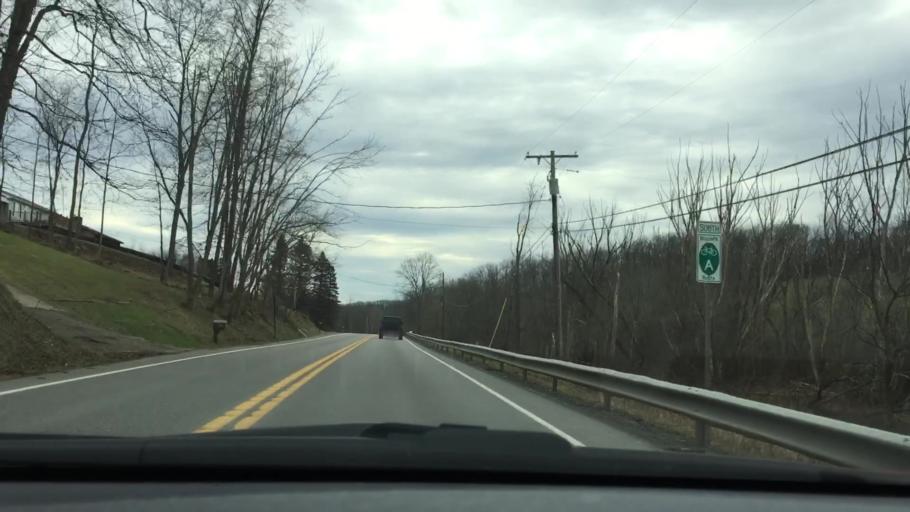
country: US
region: Pennsylvania
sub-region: Washington County
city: McDonald
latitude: 40.3466
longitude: -80.2407
